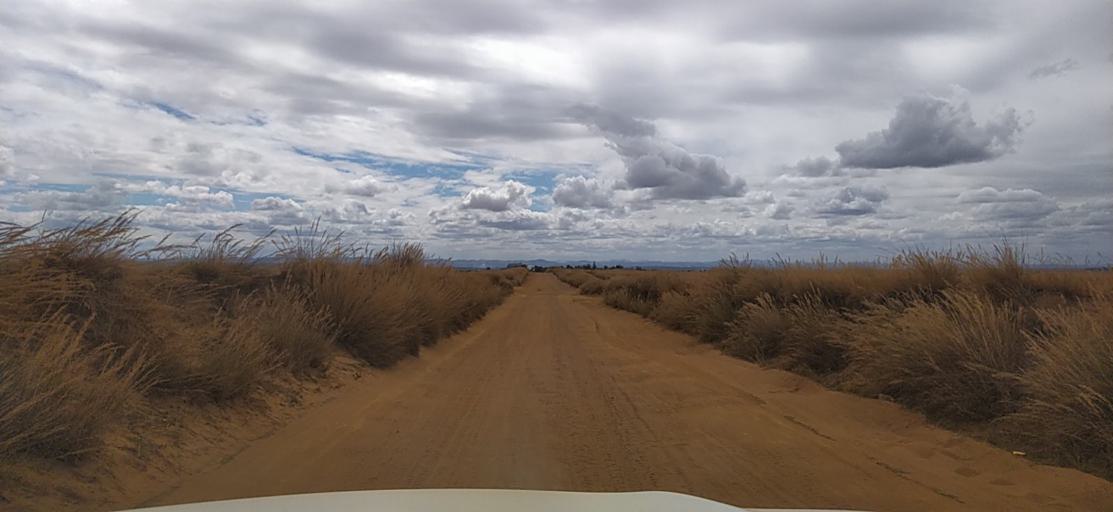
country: MG
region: Alaotra Mangoro
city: Ambatondrazaka
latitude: -17.9097
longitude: 48.2634
